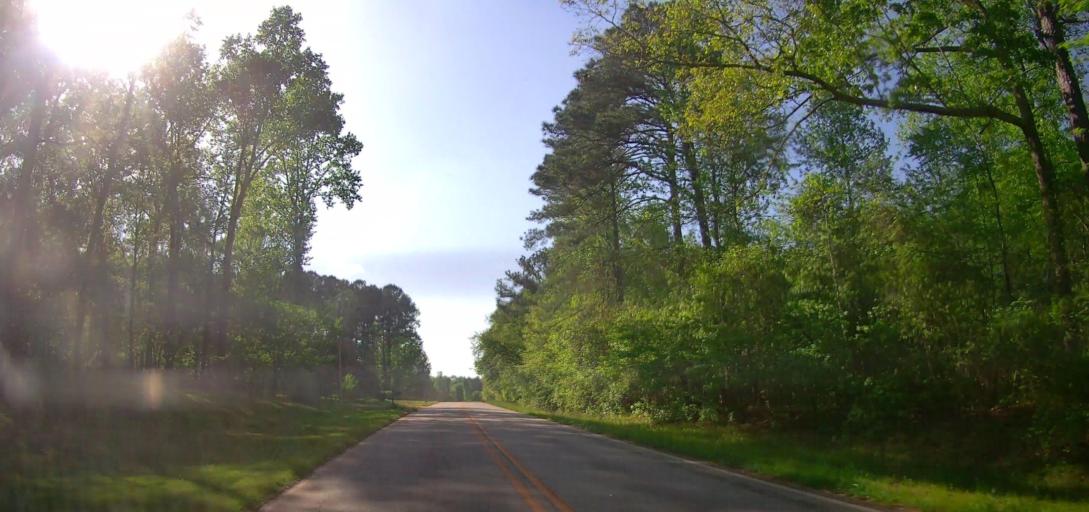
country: US
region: Georgia
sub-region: Morgan County
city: Madison
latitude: 33.5148
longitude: -83.4978
